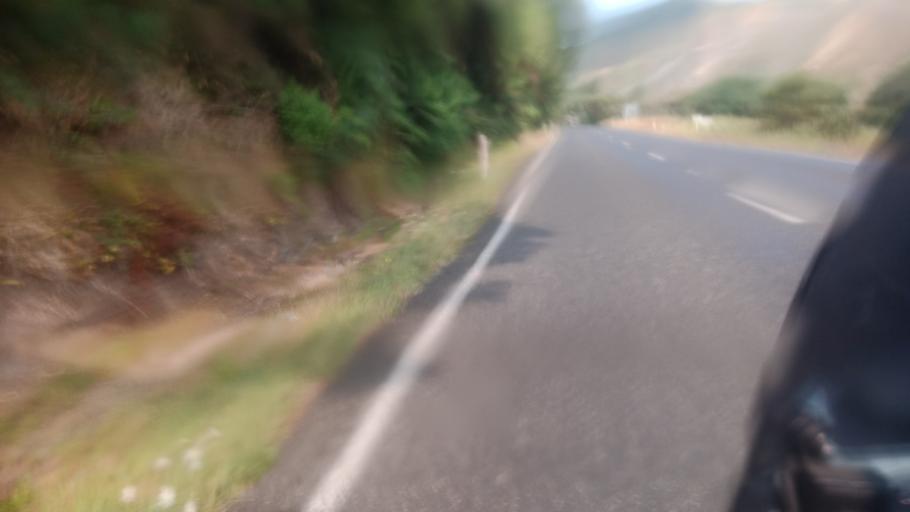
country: NZ
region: Bay of Plenty
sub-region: Opotiki District
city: Opotiki
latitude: -37.7984
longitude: 177.6657
